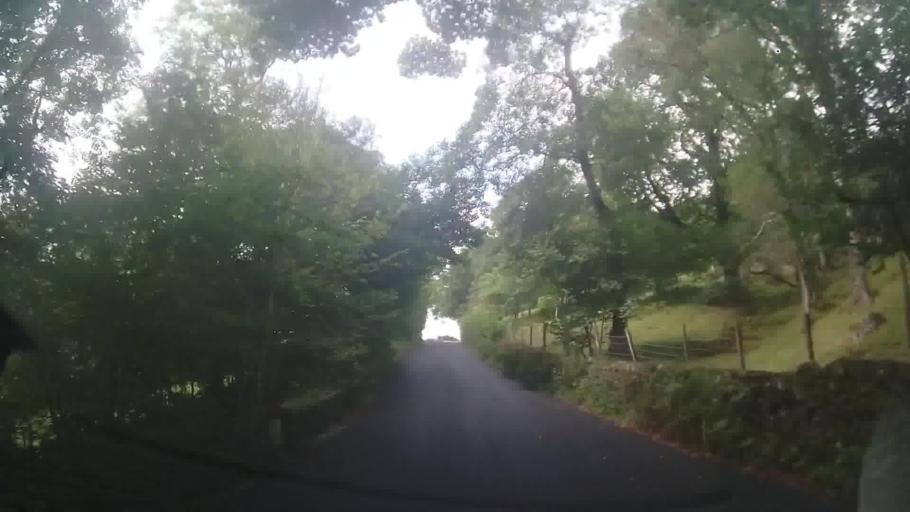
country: GB
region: England
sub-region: Cumbria
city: Ambleside
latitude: 54.4188
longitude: -3.0465
